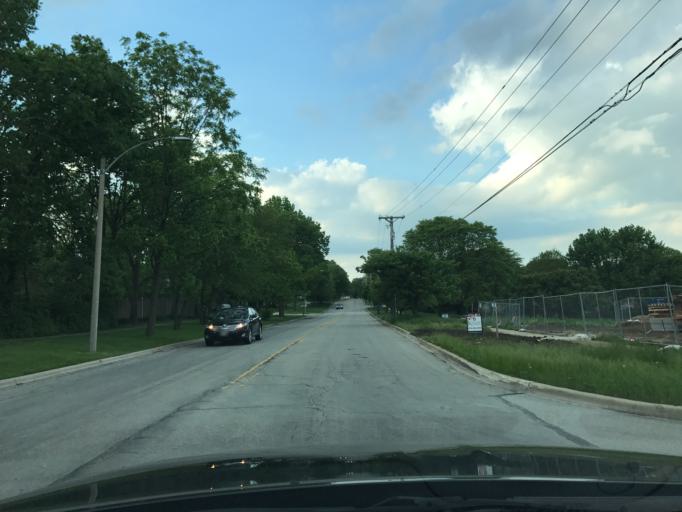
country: US
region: Illinois
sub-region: DuPage County
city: Naperville
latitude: 41.7651
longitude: -88.1209
